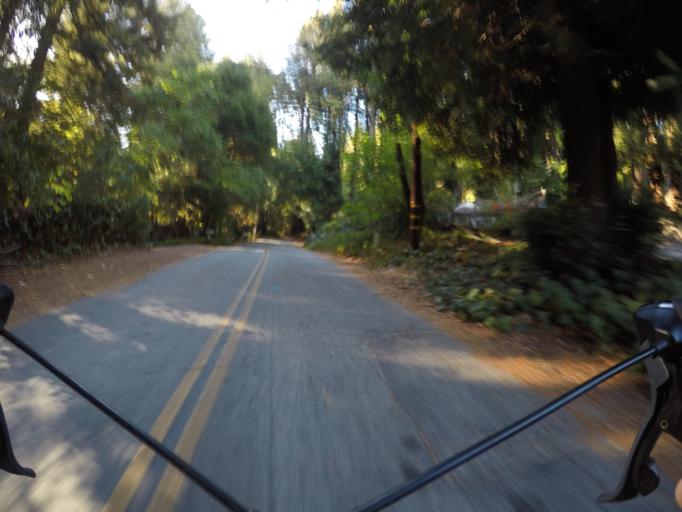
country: US
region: California
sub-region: Santa Cruz County
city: Boulder Creek
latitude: 37.1198
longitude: -122.1171
